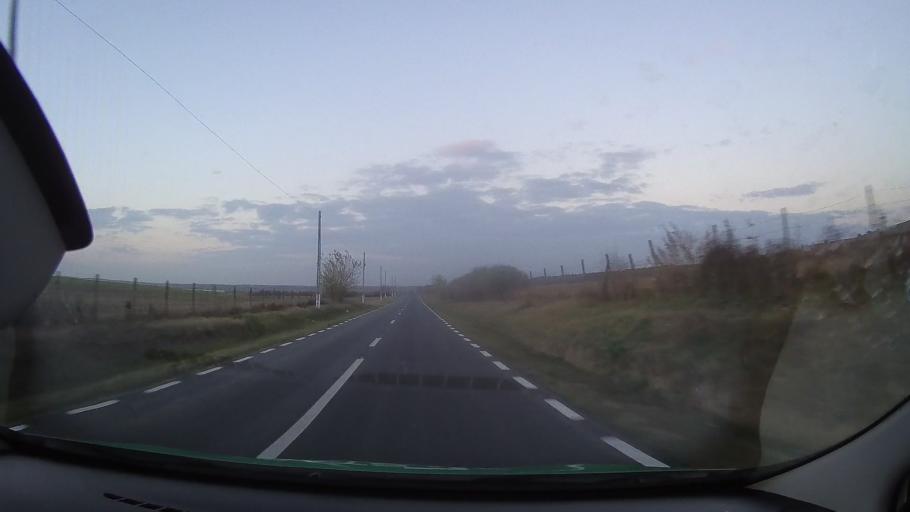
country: RO
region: Constanta
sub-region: Comuna Oltina
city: Oltina
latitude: 44.1522
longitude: 27.6677
